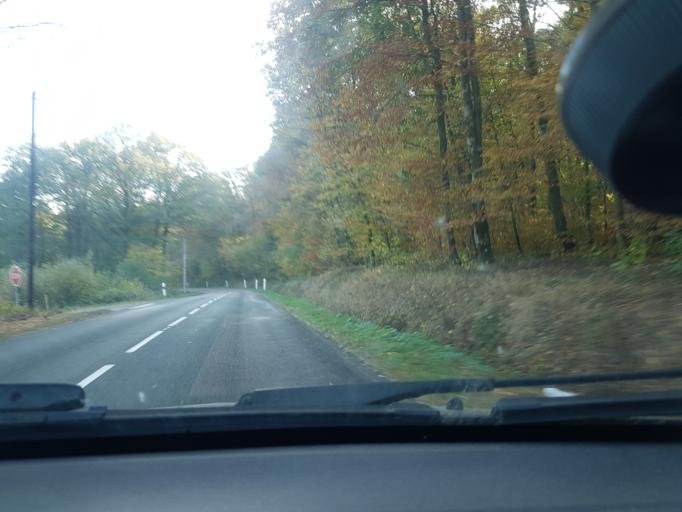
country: FR
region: Franche-Comte
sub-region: Departement de la Haute-Saone
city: Frahier-et-Chatebier
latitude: 47.6804
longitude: 6.7375
